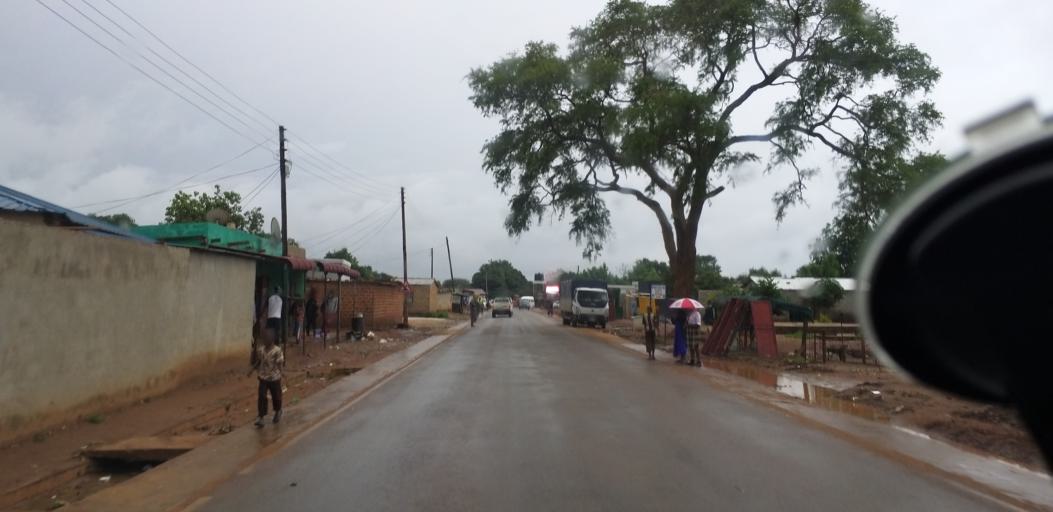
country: ZM
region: Lusaka
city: Lusaka
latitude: -15.5143
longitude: 28.2984
